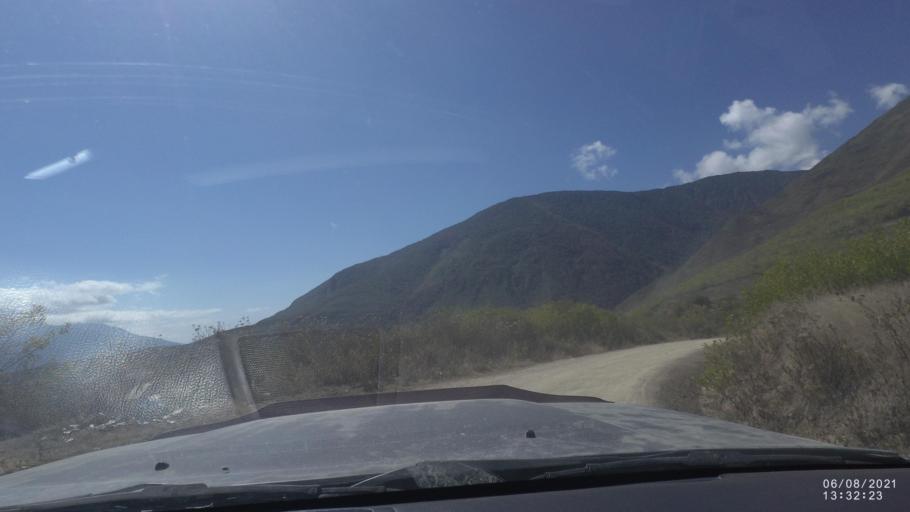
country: BO
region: La Paz
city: Quime
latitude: -16.6989
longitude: -66.7277
